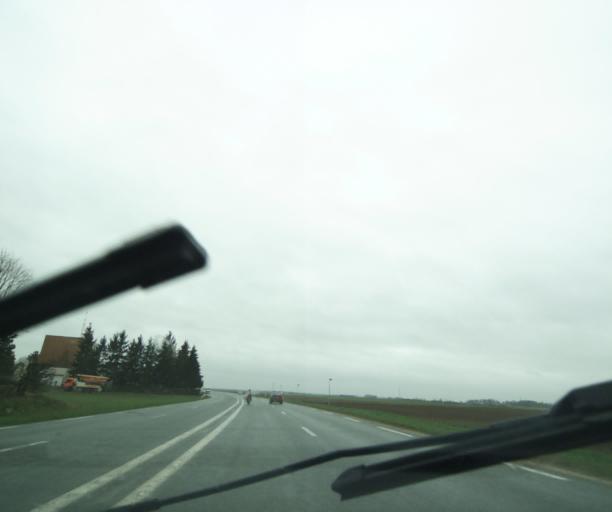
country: FR
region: Centre
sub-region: Departement du Loiret
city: Artenay
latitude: 48.0790
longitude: 1.8735
